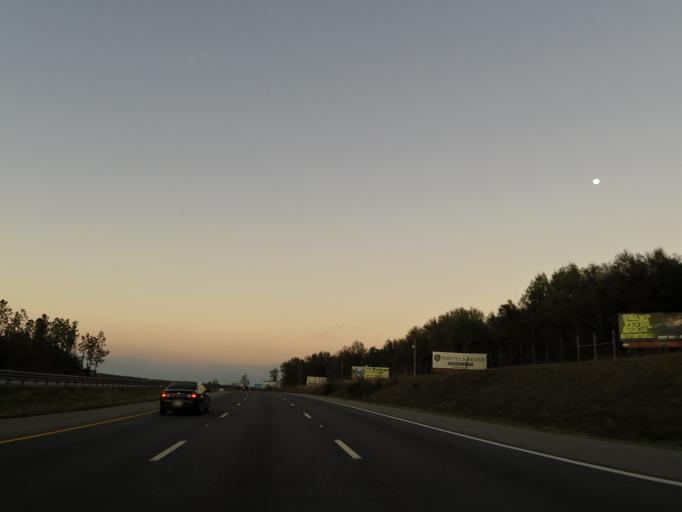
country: US
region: Florida
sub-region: Hernando County
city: Hill 'n Dale
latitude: 28.4800
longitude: -82.2509
